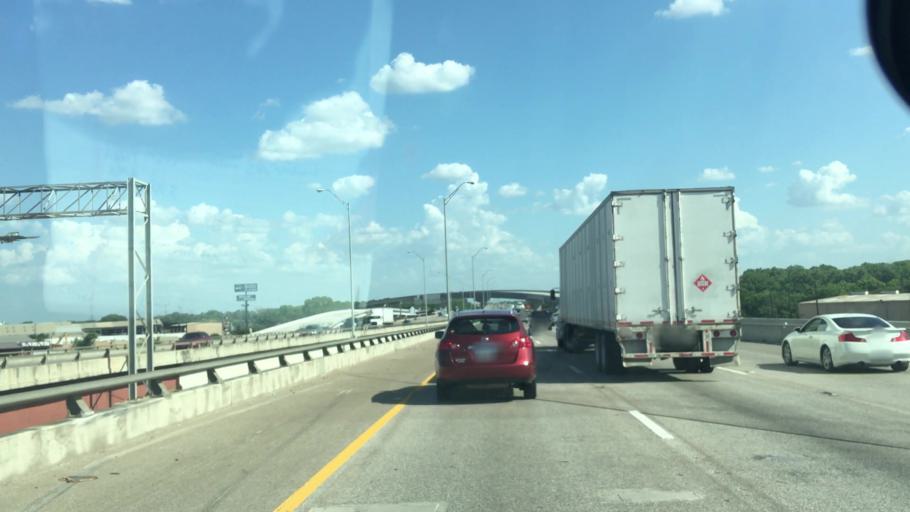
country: US
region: Texas
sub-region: Dallas County
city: Dallas
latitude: 32.7519
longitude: -96.7707
